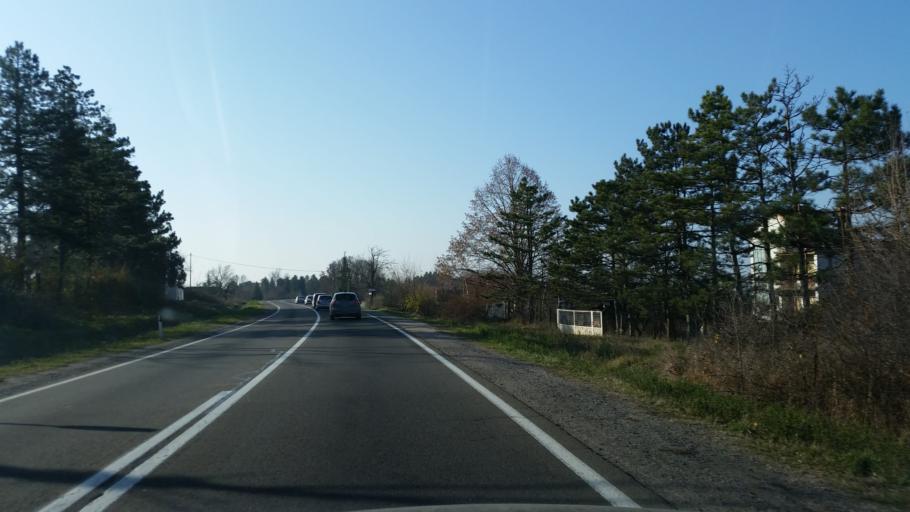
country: RS
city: Vranic
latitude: 44.5903
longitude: 20.3443
